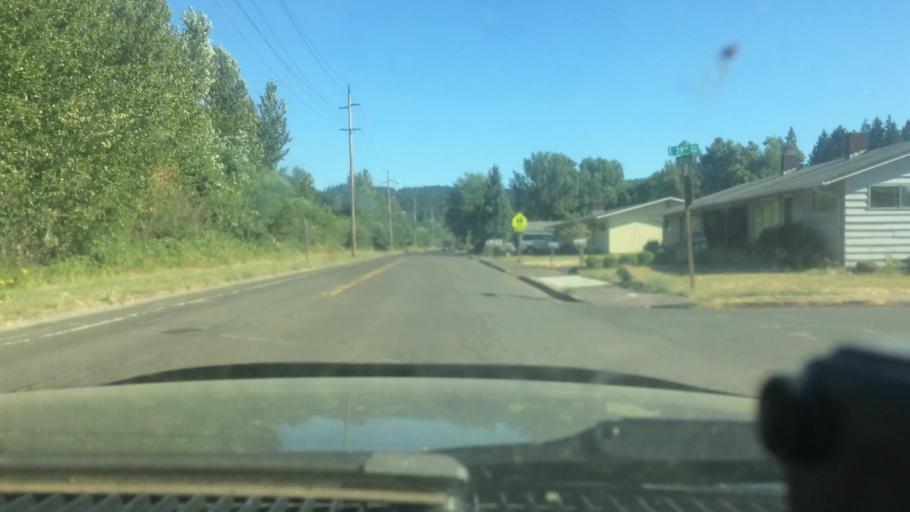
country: US
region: Oregon
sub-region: Lane County
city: Eugene
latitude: 44.0144
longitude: -123.0783
